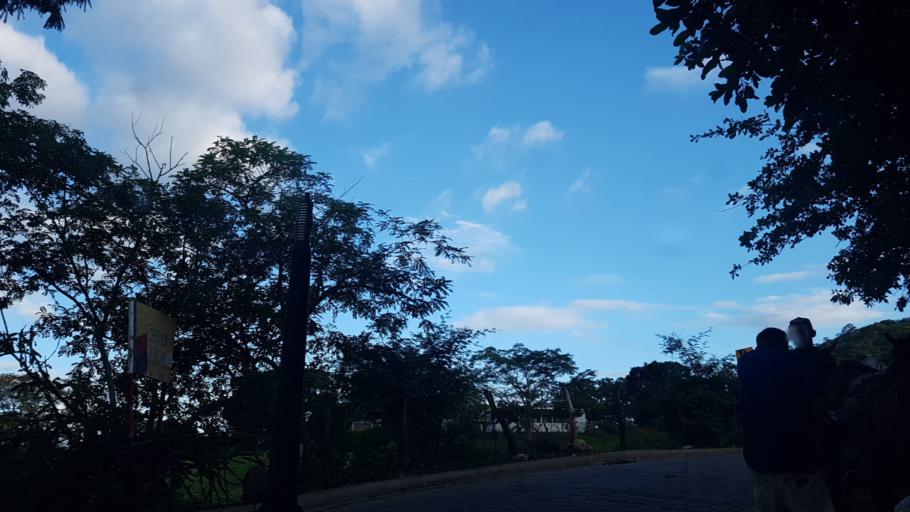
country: NI
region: Nueva Segovia
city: Ocotal
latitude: 13.6518
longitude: -86.6117
